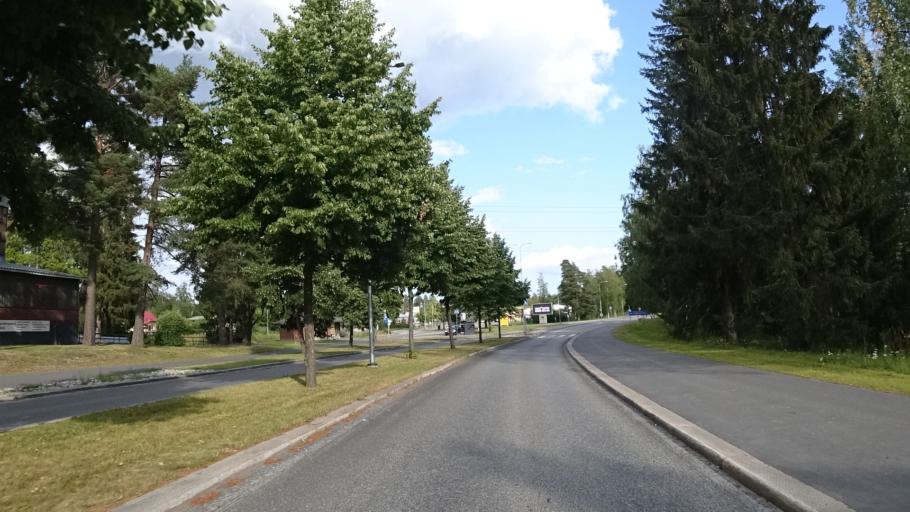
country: FI
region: South Karelia
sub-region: Imatra
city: Imatra
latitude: 61.1721
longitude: 28.7505
